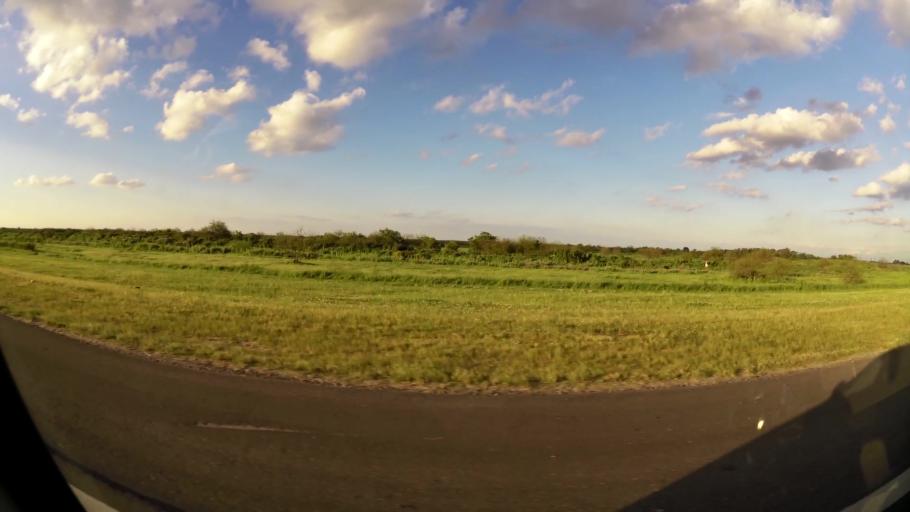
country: AR
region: Buenos Aires
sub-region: Partido de La Plata
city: La Plata
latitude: -34.8722
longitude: -57.9805
